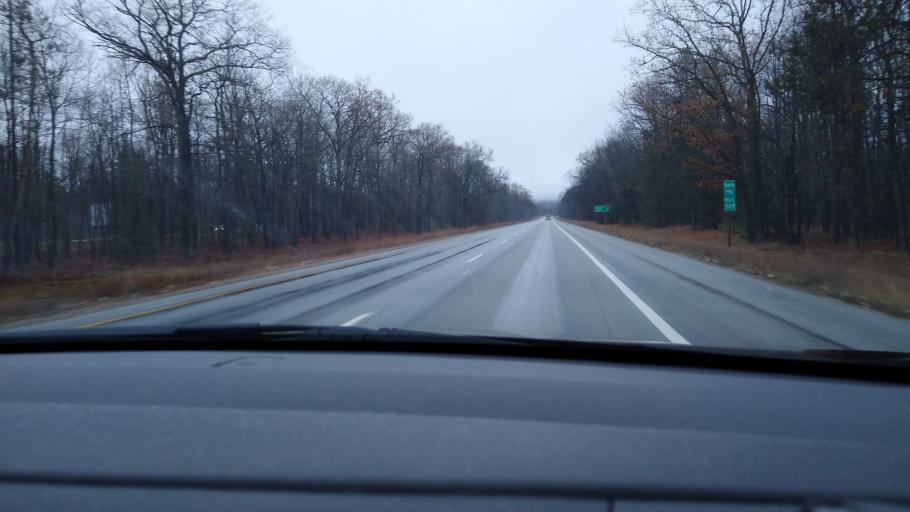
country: US
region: Michigan
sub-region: Cheboygan County
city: Indian River
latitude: 45.3897
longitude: -84.6072
